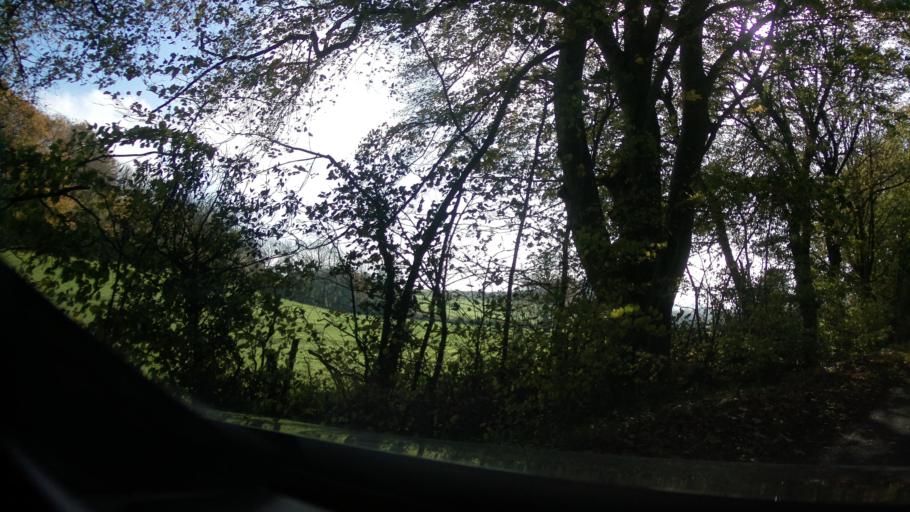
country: GB
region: England
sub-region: Somerset
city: Castle Cary
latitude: 51.0563
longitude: -2.4823
